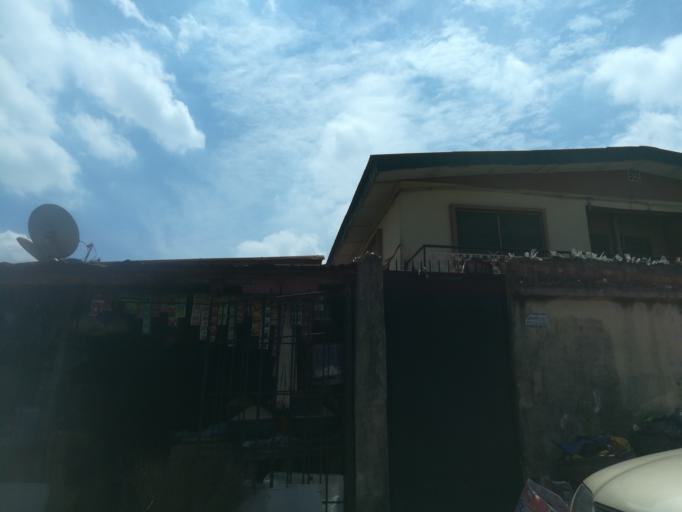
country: NG
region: Lagos
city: Oshodi
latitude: 6.5664
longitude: 3.3345
